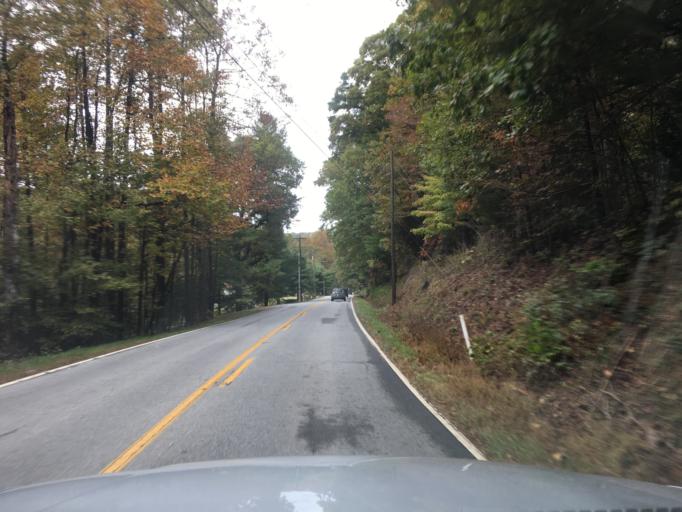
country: US
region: North Carolina
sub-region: Henderson County
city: Flat Rock
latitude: 35.2509
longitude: -82.4294
